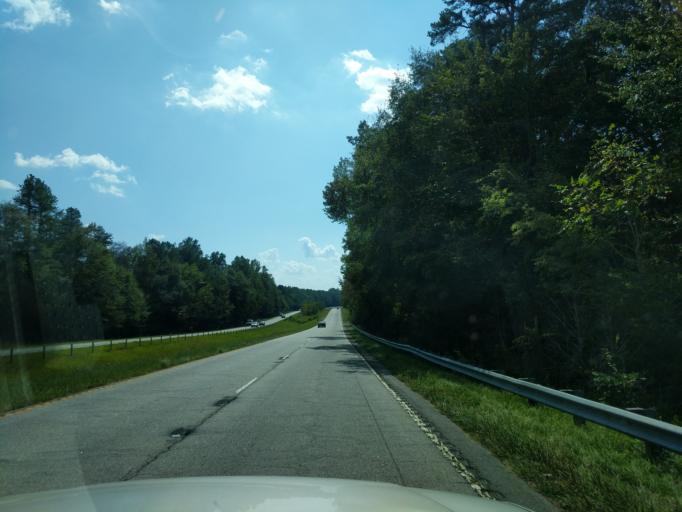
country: US
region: South Carolina
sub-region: Pickens County
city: Central
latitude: 34.7147
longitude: -82.7484
